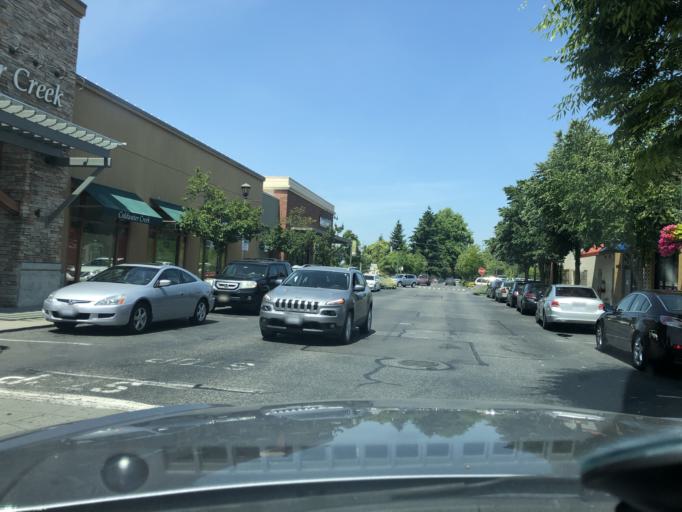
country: US
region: Washington
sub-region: King County
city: Kent
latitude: 47.3851
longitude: -122.2356
